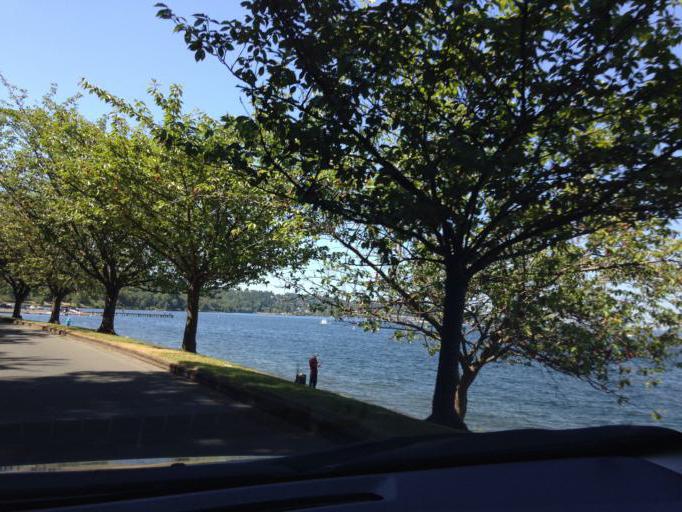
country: US
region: Washington
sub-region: King County
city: Mercer Island
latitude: 47.5696
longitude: -122.2744
